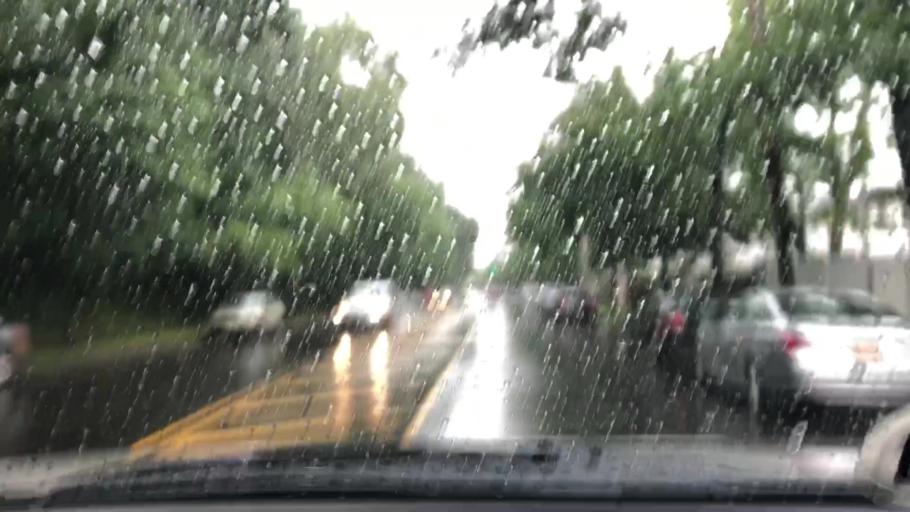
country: US
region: New Jersey
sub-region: Middlesex County
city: Carteret
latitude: 40.5496
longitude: -74.2005
